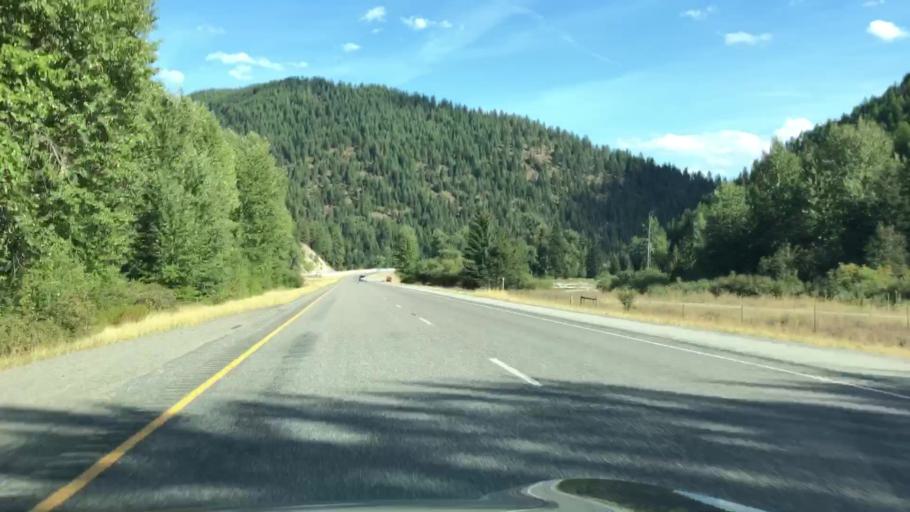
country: US
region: Montana
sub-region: Sanders County
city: Thompson Falls
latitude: 47.3568
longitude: -115.3015
